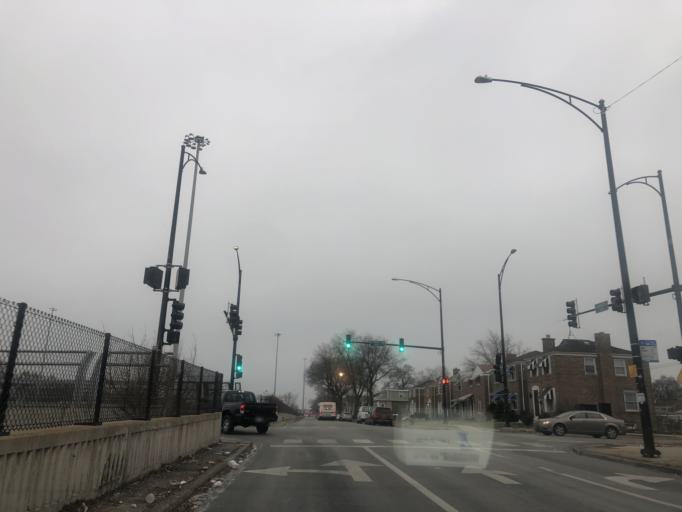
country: US
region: Illinois
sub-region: Cook County
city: Calumet Park
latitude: 41.7294
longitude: -87.6253
